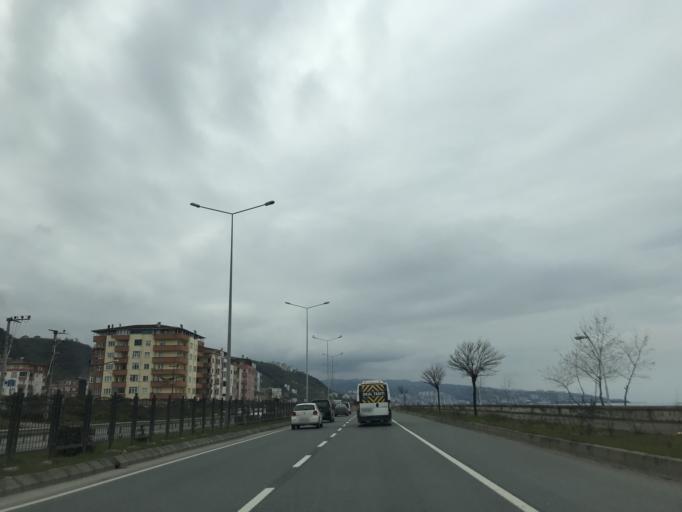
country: TR
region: Trabzon
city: Arsin
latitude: 40.9546
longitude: 39.9212
